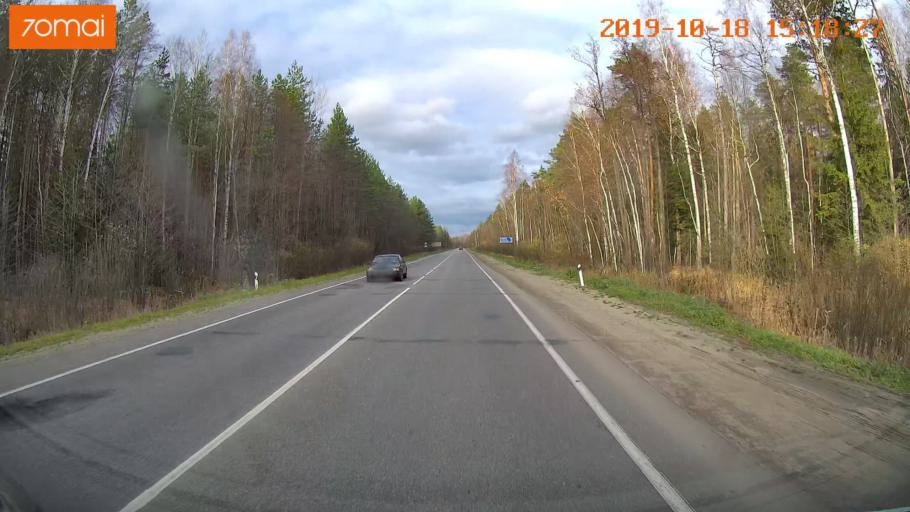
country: RU
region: Vladimir
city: Anopino
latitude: 55.6595
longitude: 40.7289
